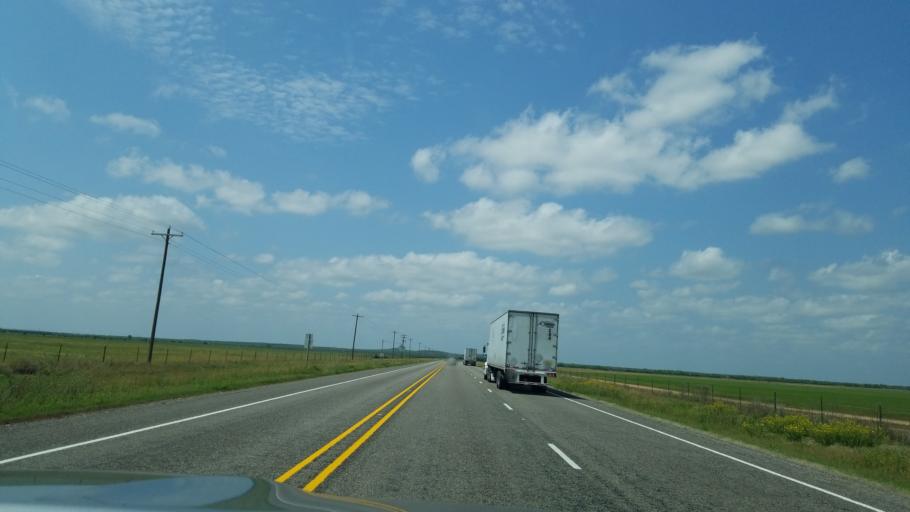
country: US
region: Texas
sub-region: Frio County
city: Pearsall
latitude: 28.9694
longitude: -99.2464
